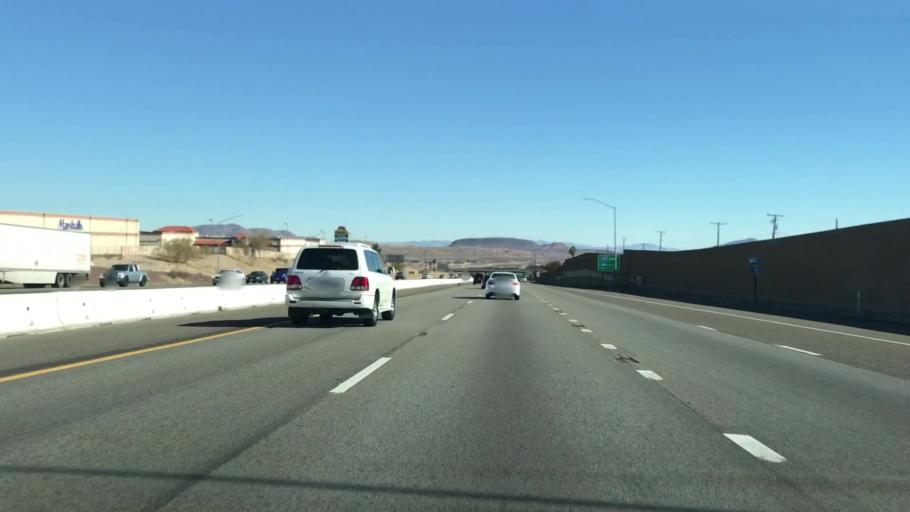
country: US
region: California
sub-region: San Bernardino County
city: Barstow
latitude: 34.8854
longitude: -117.0207
